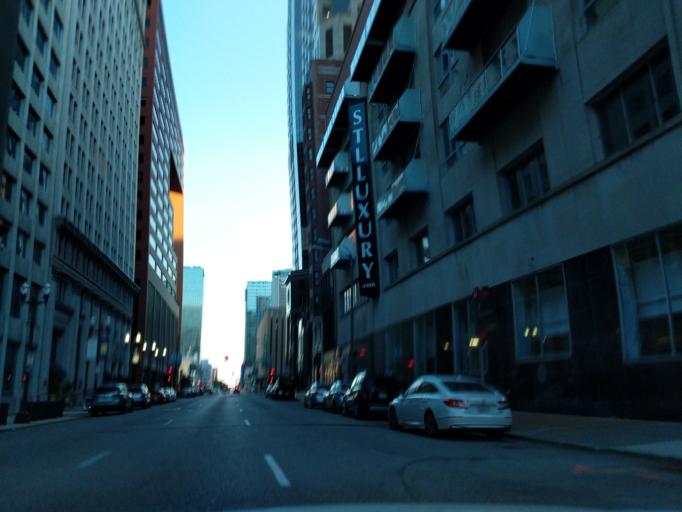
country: US
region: Missouri
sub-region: City of Saint Louis
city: St. Louis
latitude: 38.6285
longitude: -90.1888
